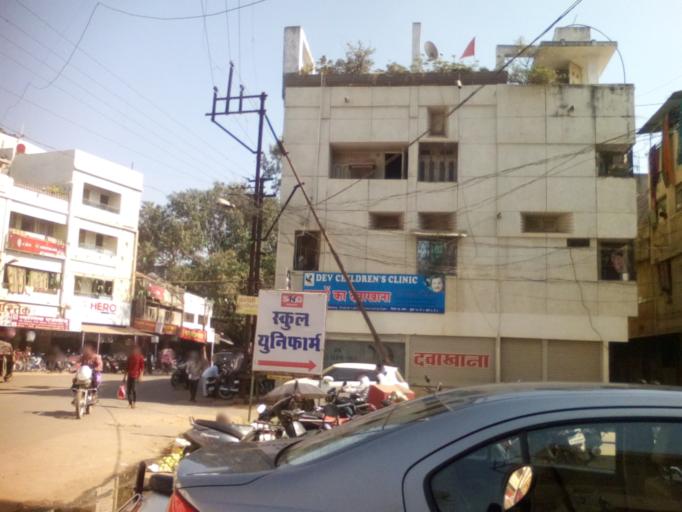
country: IN
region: Maharashtra
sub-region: Gondiya
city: Gondia
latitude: 21.4558
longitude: 80.1927
